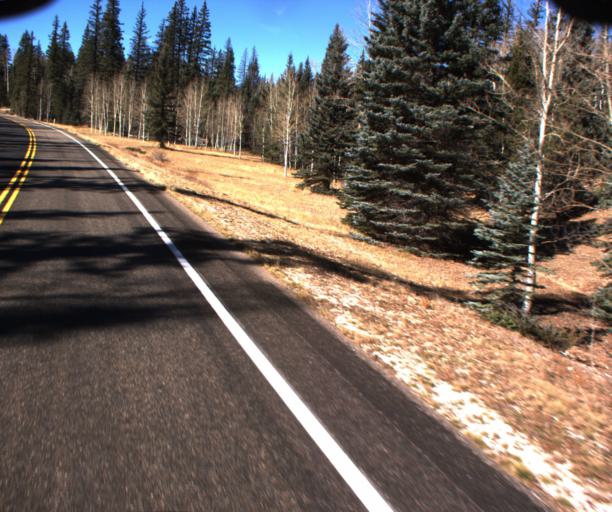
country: US
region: Arizona
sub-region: Coconino County
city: Grand Canyon
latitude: 36.5239
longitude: -112.1423
